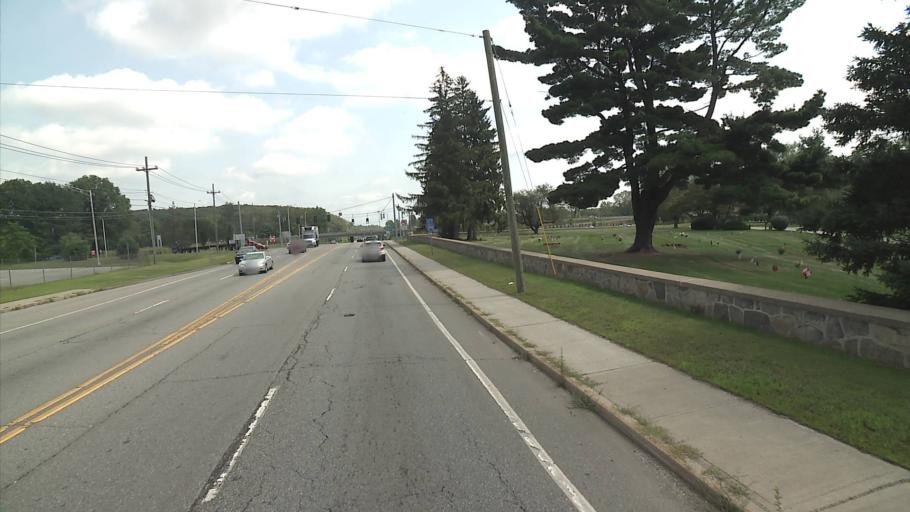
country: US
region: Connecticut
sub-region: New London County
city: Montville Center
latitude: 41.5087
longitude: -72.1187
